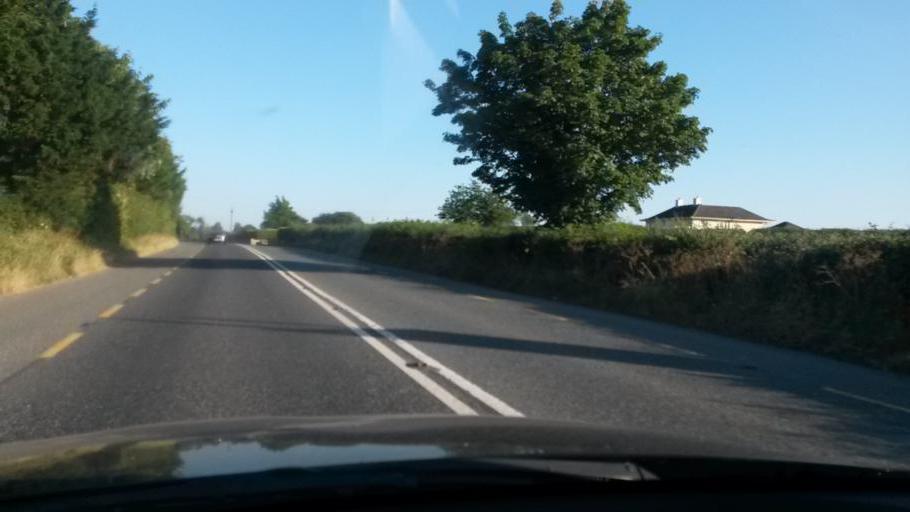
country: IE
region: Leinster
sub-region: Fingal County
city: Blanchardstown
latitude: 53.4425
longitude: -6.3399
